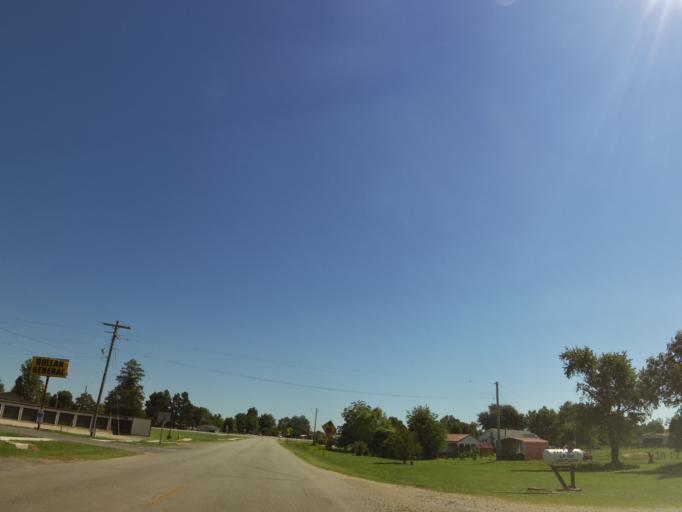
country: US
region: Missouri
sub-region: Dunklin County
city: Campbell
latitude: 36.4965
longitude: -90.0703
